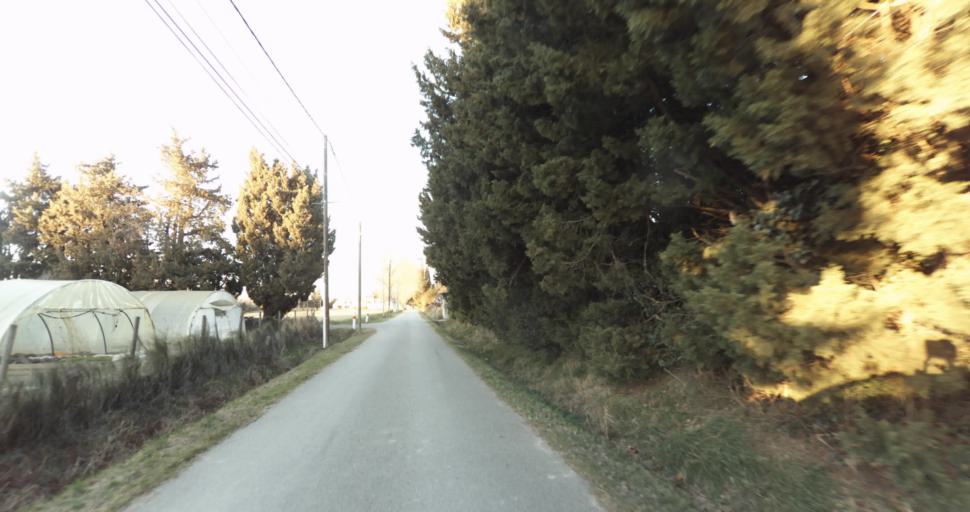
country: FR
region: Provence-Alpes-Cote d'Azur
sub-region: Departement des Bouches-du-Rhone
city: Rognonas
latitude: 43.8990
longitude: 4.7830
